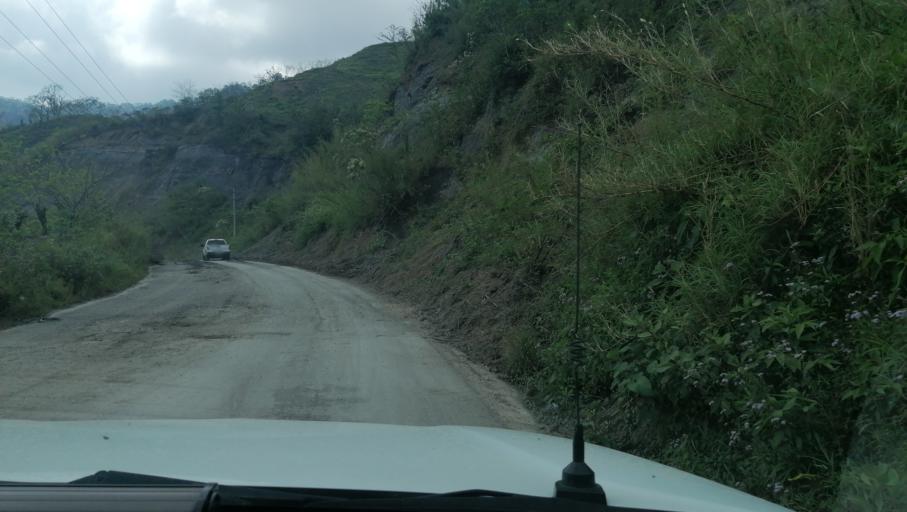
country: MX
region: Chiapas
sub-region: Ocotepec
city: San Pablo Huacano
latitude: 17.2658
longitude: -93.2639
